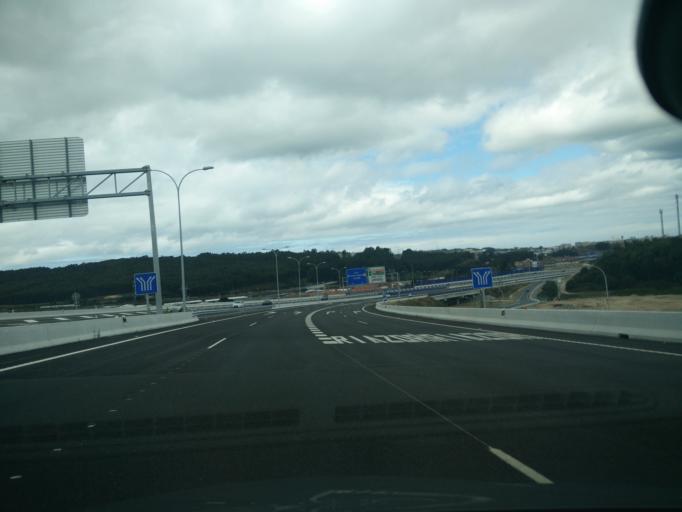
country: ES
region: Galicia
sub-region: Provincia da Coruna
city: Culleredo
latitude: 43.3265
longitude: -8.4221
